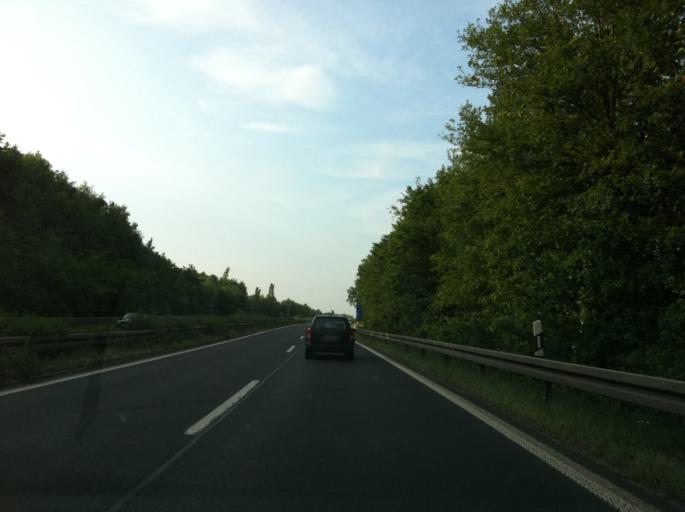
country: DE
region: Bavaria
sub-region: Regierungsbezirk Unterfranken
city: Kleinostheim
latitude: 49.9842
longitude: 9.0515
